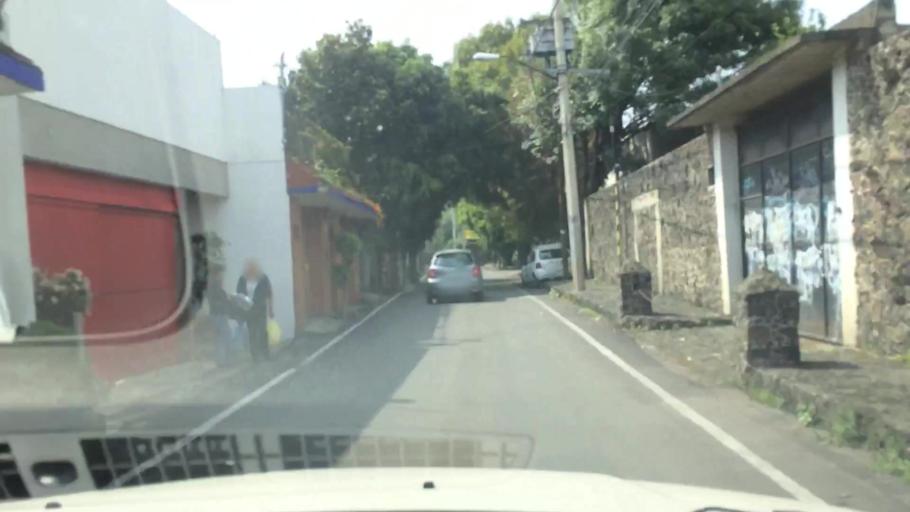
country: MX
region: Mexico City
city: Xochimilco
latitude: 19.2690
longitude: -99.1414
